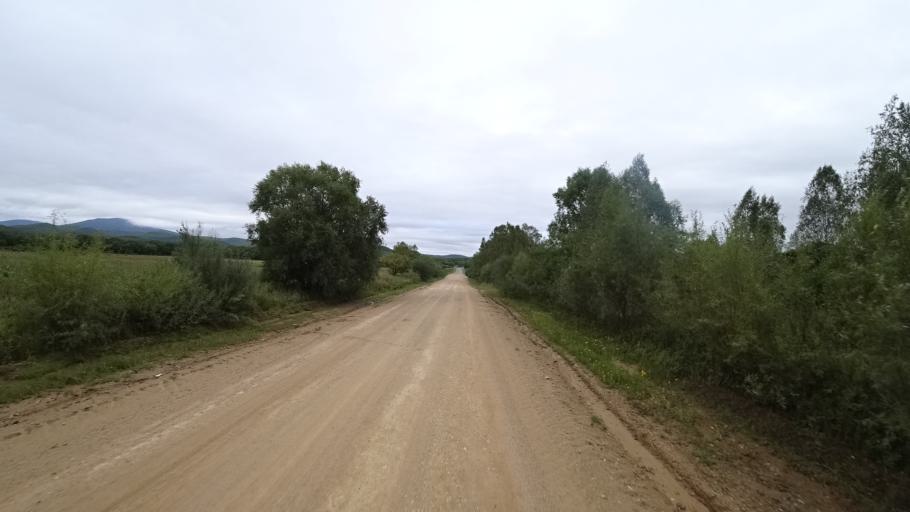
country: RU
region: Primorskiy
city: Rettikhovka
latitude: 44.1596
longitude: 132.7125
